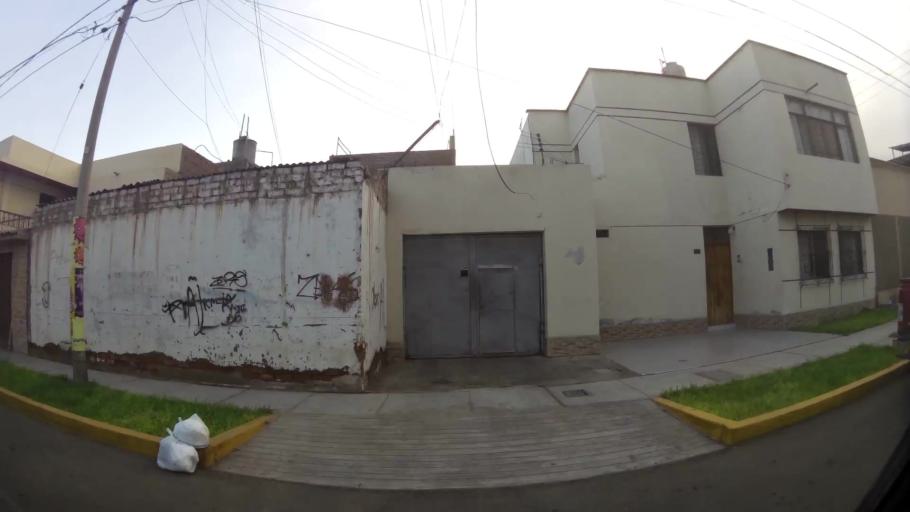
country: PE
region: La Libertad
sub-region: Provincia de Trujillo
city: La Esperanza
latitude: -8.0959
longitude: -79.0379
